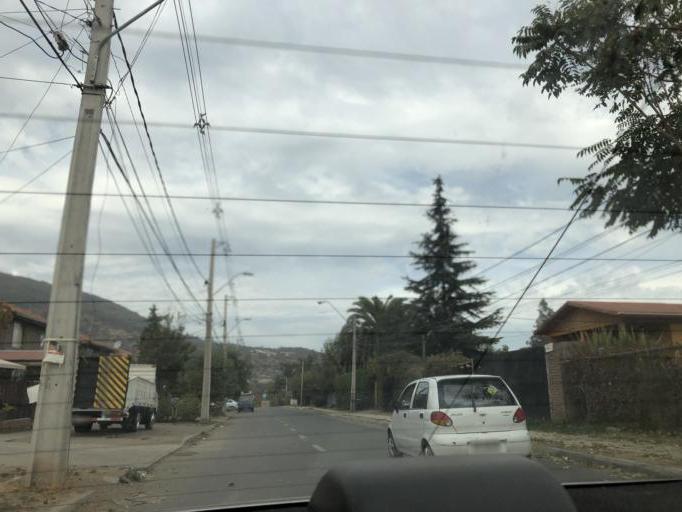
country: CL
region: Santiago Metropolitan
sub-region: Provincia de Cordillera
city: Puente Alto
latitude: -33.6121
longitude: -70.5308
